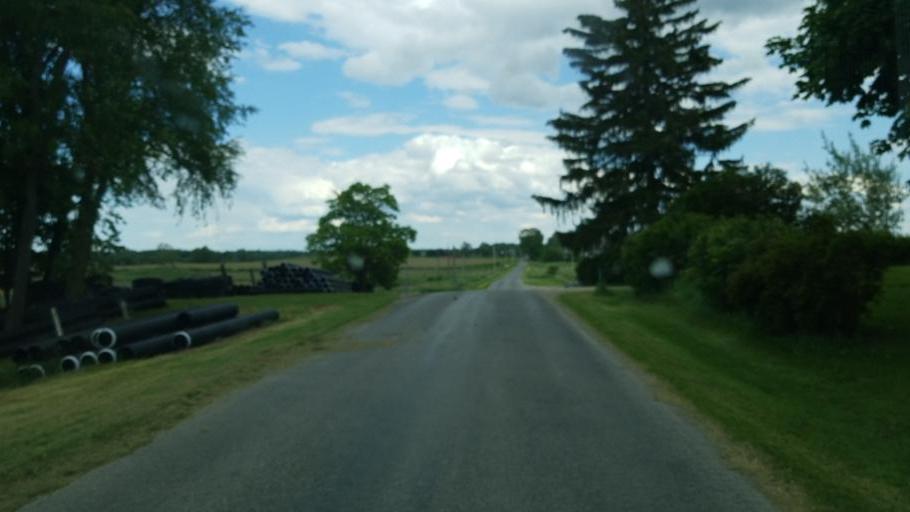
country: US
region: Ohio
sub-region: Richland County
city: Shelby
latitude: 40.9380
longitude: -82.6123
